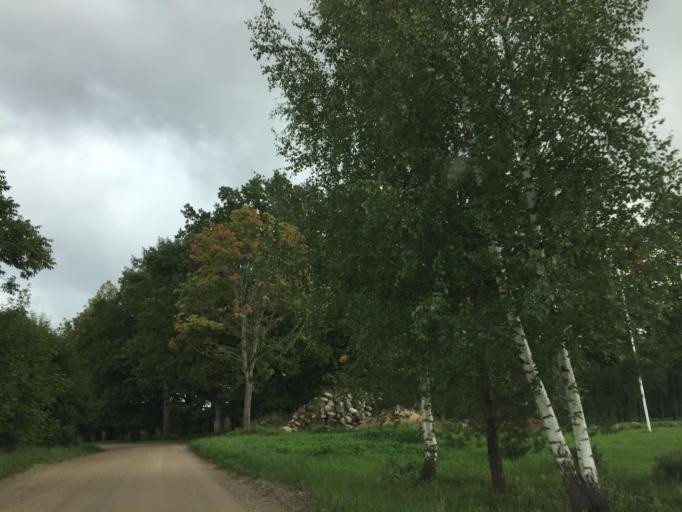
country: LV
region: Priekuli
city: Priekuli
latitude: 57.3698
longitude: 25.4357
